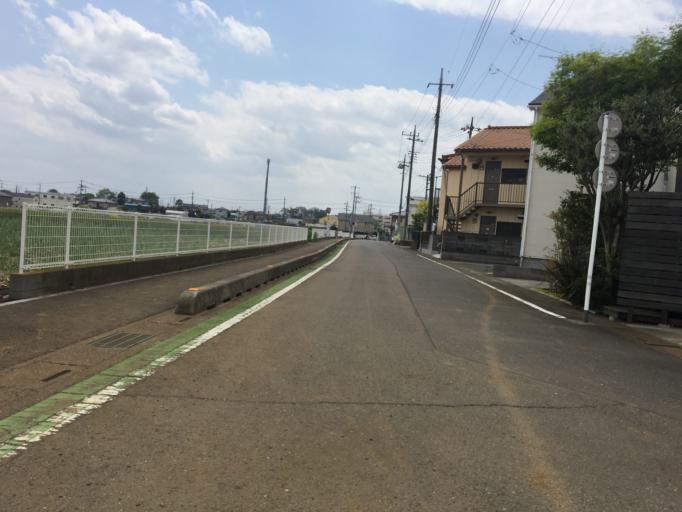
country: JP
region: Saitama
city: Oi
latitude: 35.8317
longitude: 139.5461
